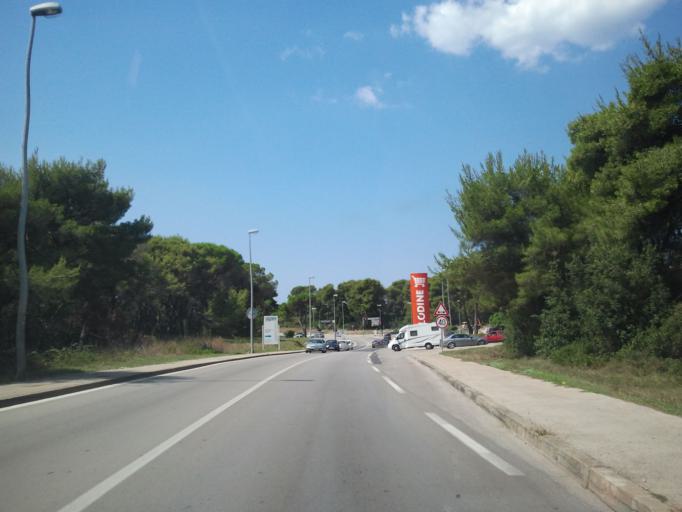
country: HR
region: Zadarska
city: Zadar
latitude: 44.1394
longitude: 15.2312
